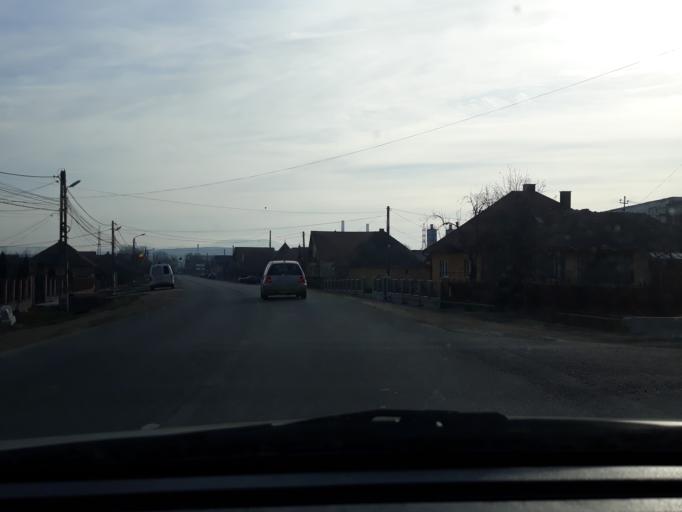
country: RO
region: Salaj
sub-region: Comuna Criseni
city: Criseni
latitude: 47.2270
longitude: 23.0397
